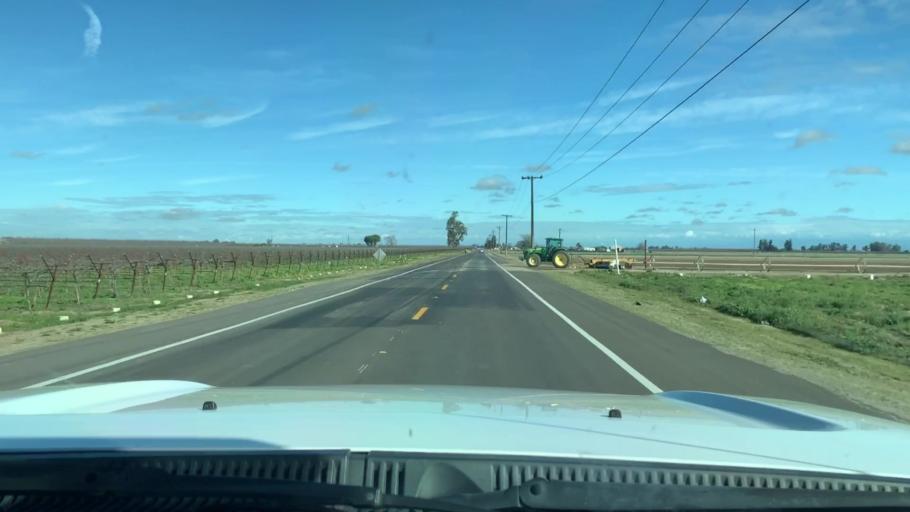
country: US
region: California
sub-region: Fresno County
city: Laton
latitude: 36.5049
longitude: -119.6830
